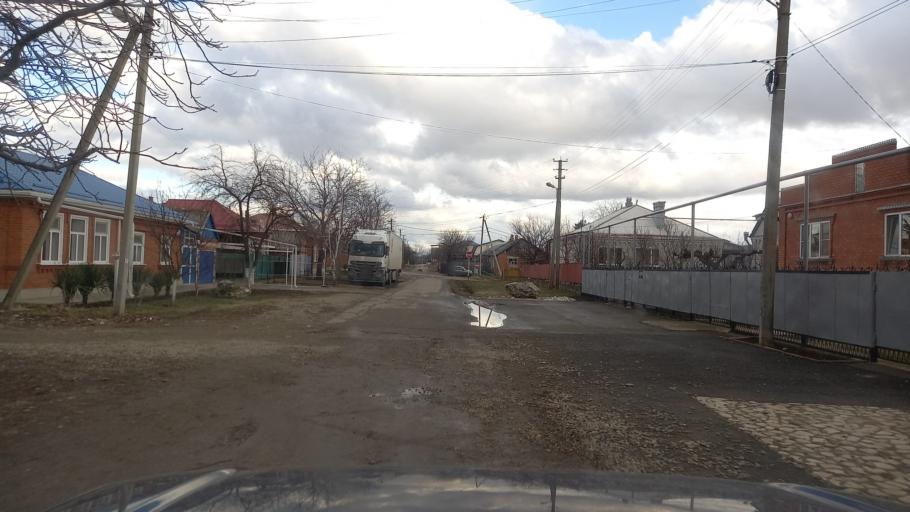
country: RU
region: Adygeya
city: Maykop
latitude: 44.5961
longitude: 40.0658
